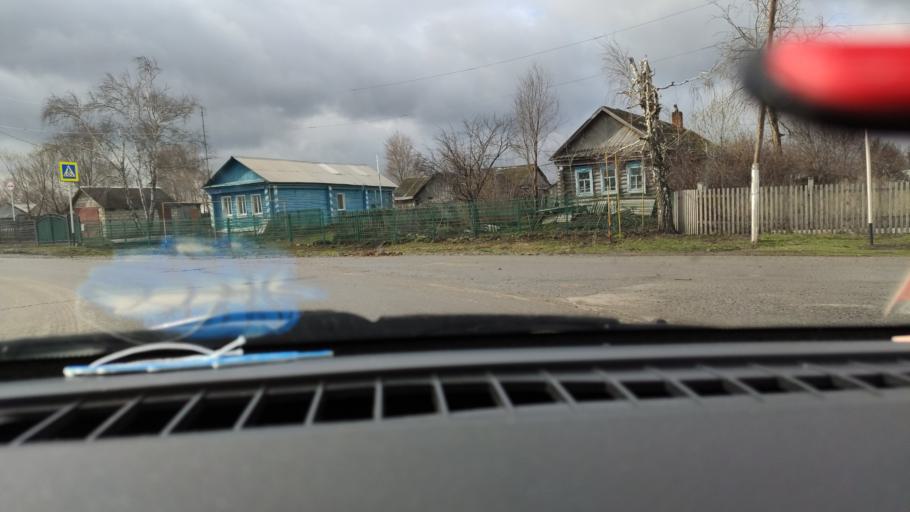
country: RU
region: Samara
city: Koshki
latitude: 54.2701
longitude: 50.6353
